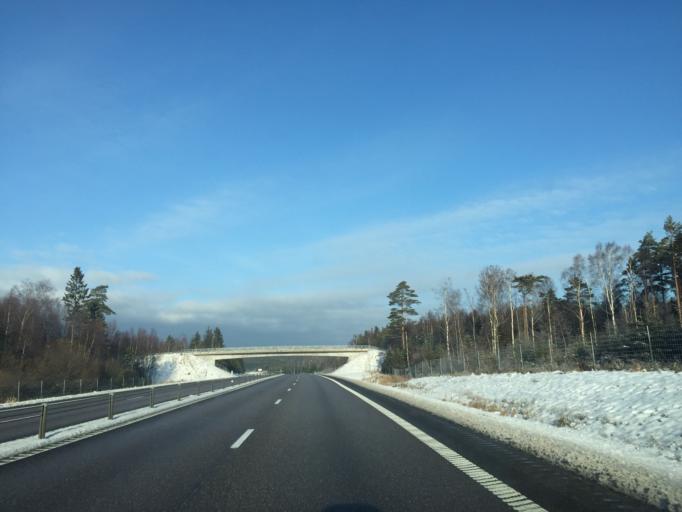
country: SE
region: Vaestra Goetaland
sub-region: Tanums Kommun
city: Tanumshede
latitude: 58.7434
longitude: 11.3003
